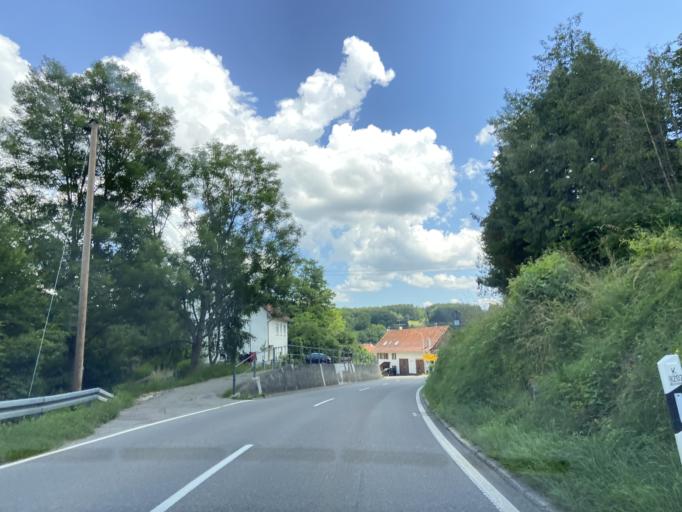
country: DE
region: Baden-Wuerttemberg
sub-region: Tuebingen Region
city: Veringenstadt
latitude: 48.1596
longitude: 9.1974
